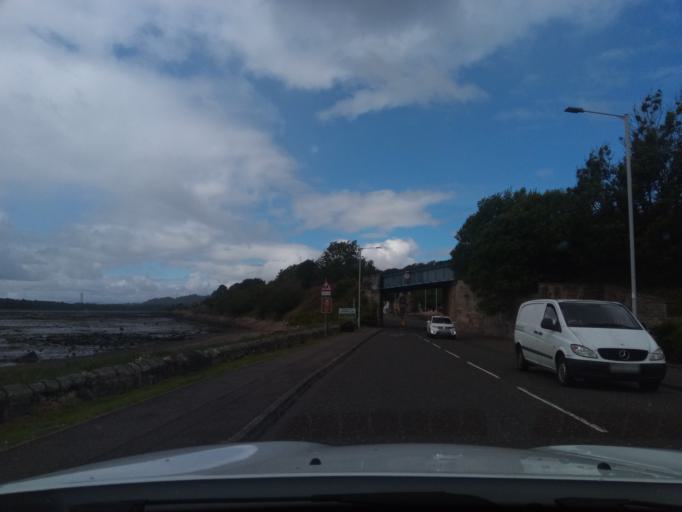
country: GB
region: Scotland
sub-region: Fife
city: High Valleyfield
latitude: 56.0587
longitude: -3.5746
